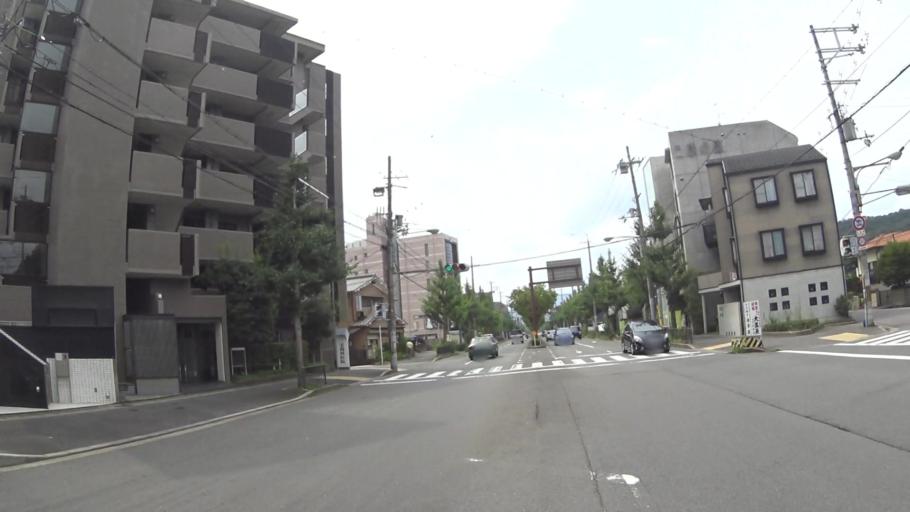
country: JP
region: Kyoto
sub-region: Kyoto-shi
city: Kamigyo-ku
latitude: 35.0519
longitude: 135.7875
